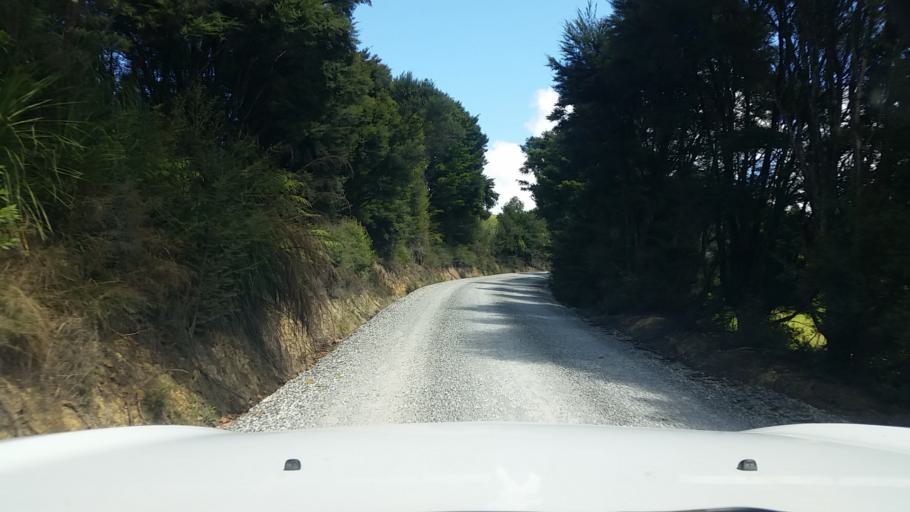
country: NZ
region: Northland
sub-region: Whangarei
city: Ngunguru
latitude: -35.6123
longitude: 174.4923
